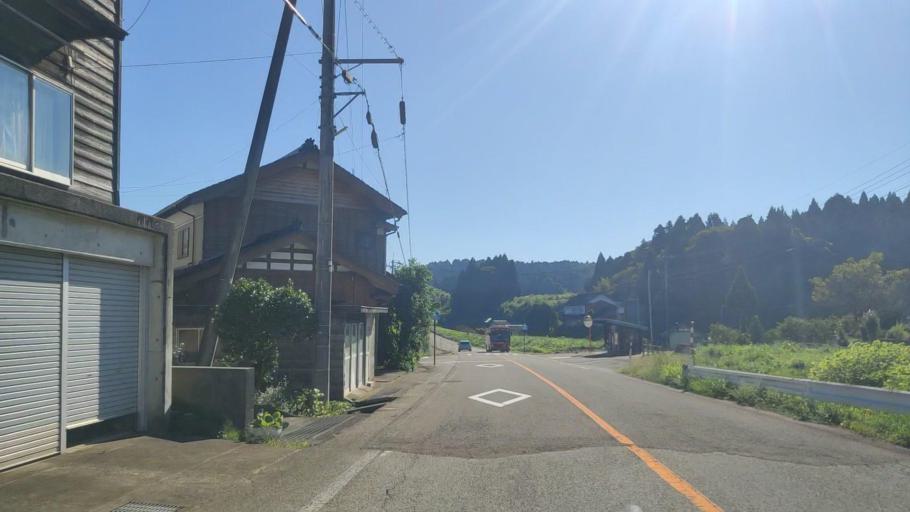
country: JP
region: Ishikawa
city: Nanao
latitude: 37.2648
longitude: 137.0909
